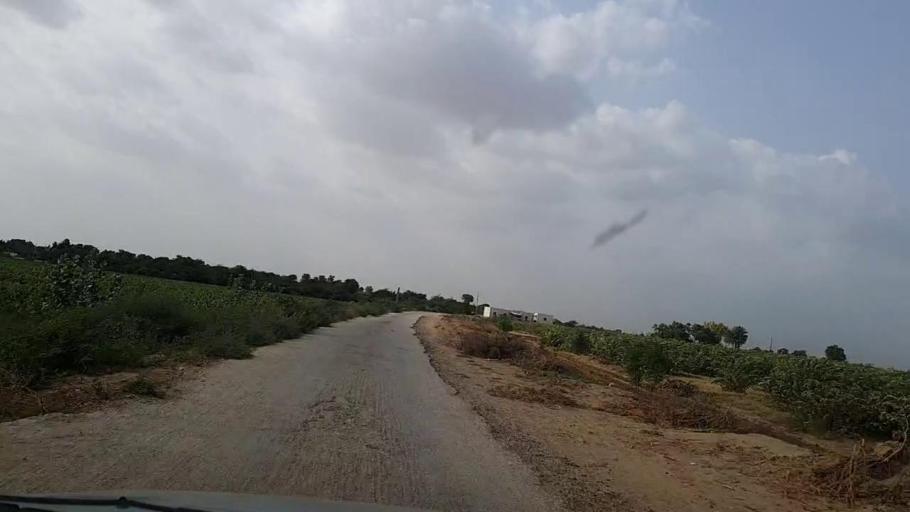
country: PK
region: Sindh
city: Kotri
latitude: 25.2540
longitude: 68.2570
